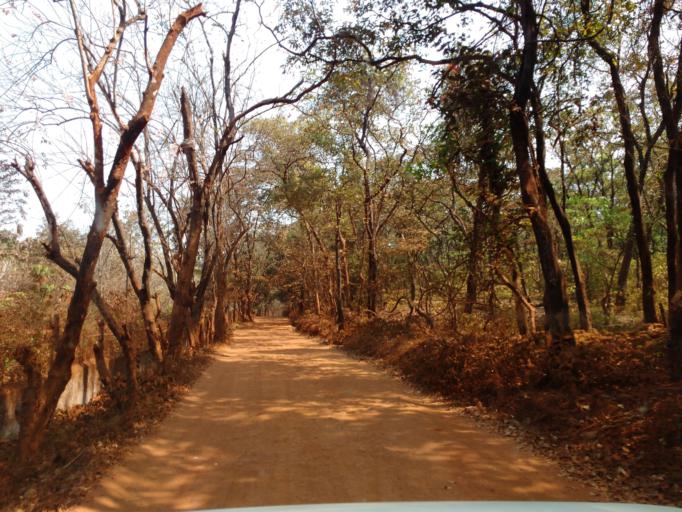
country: IN
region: Goa
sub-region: South Goa
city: Sanguem
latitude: 15.3402
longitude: 74.2504
